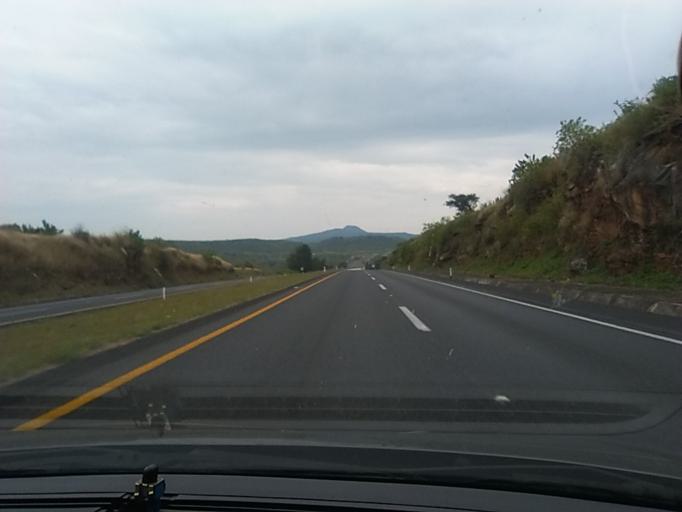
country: MX
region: Michoacan
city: Penjamillo de Degollado
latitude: 20.0501
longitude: -101.9537
